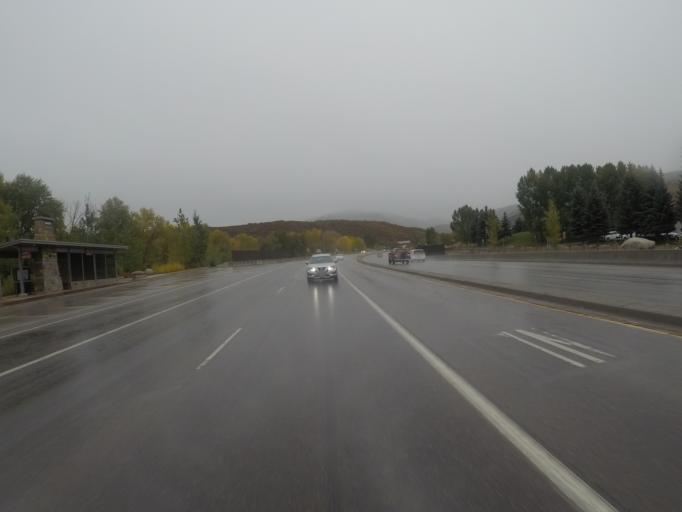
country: US
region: Colorado
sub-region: Pitkin County
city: Aspen
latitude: 39.2201
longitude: -106.8628
